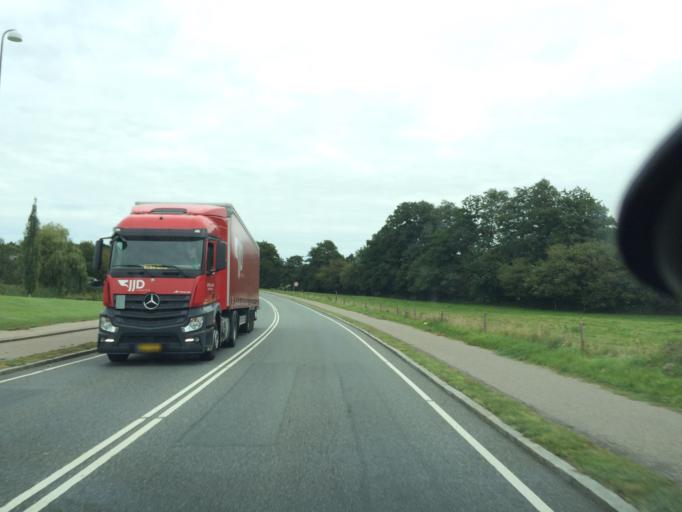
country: DK
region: South Denmark
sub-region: Aabenraa Kommune
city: Aabenraa
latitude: 55.0225
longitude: 9.4158
